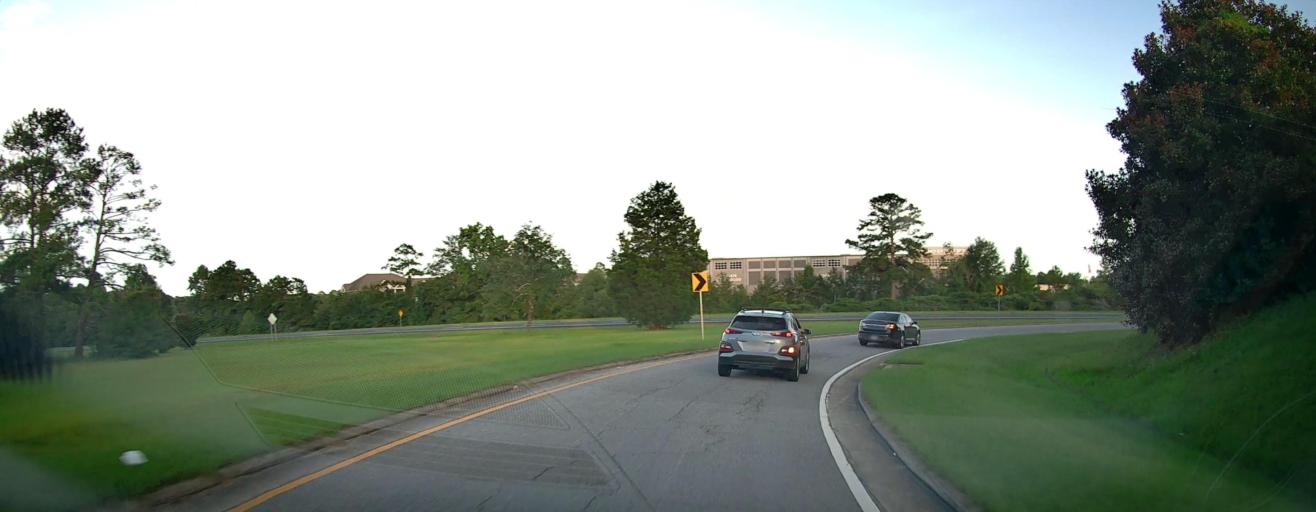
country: US
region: Georgia
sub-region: Muscogee County
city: Columbus
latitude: 32.5419
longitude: -84.8715
